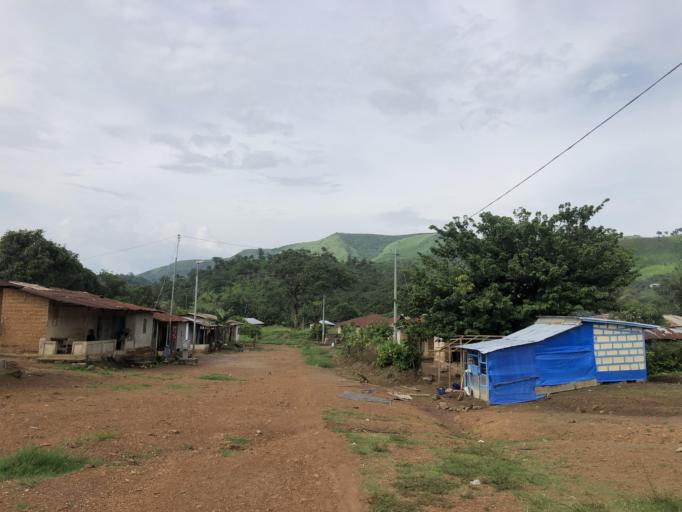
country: SL
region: Northern Province
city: Bumbuna
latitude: 9.0454
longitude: -11.7434
